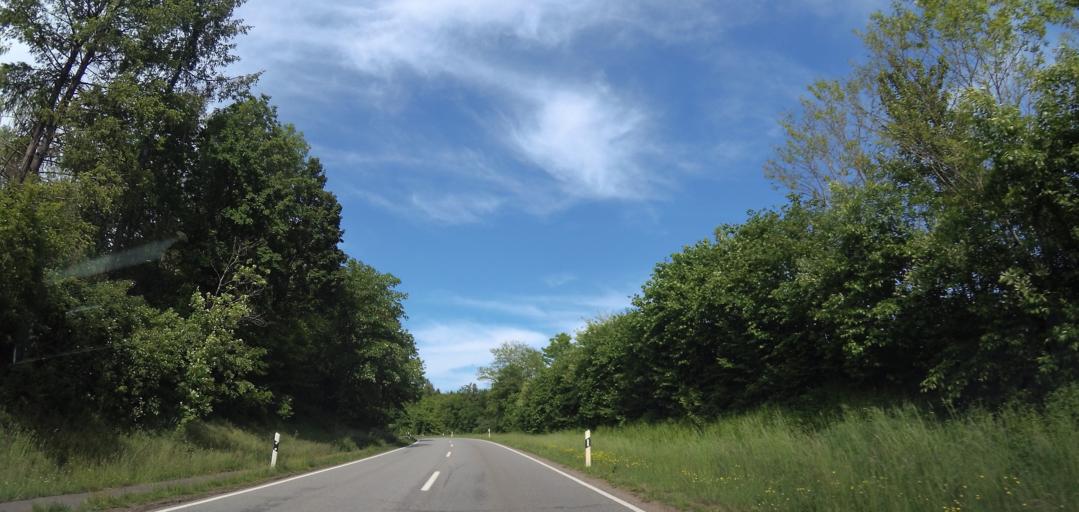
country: DE
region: Saarland
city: Schmelz
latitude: 49.4569
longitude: 6.7885
